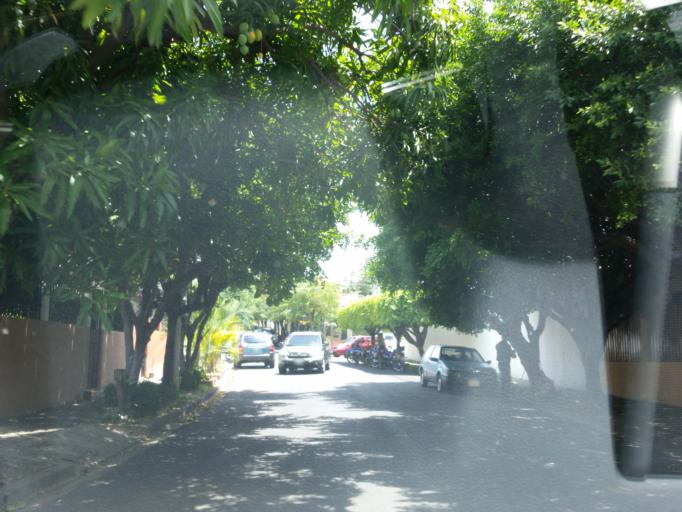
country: NI
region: Managua
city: Managua
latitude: 12.1180
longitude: -86.2688
